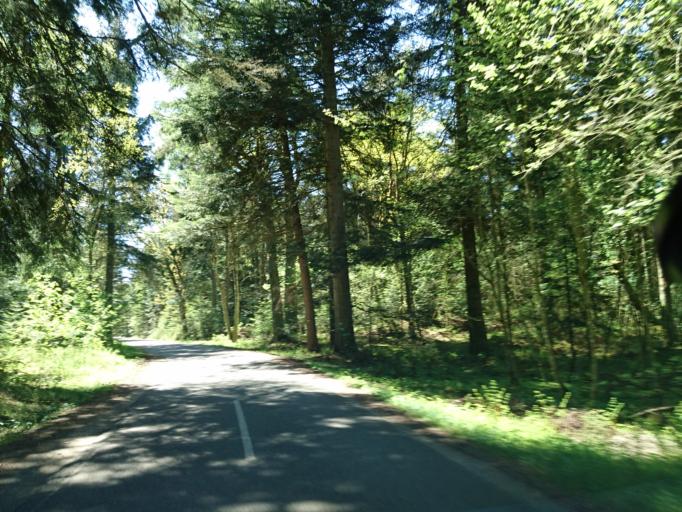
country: DK
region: North Denmark
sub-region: Hjorring Kommune
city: Sindal
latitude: 57.5981
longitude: 10.2307
